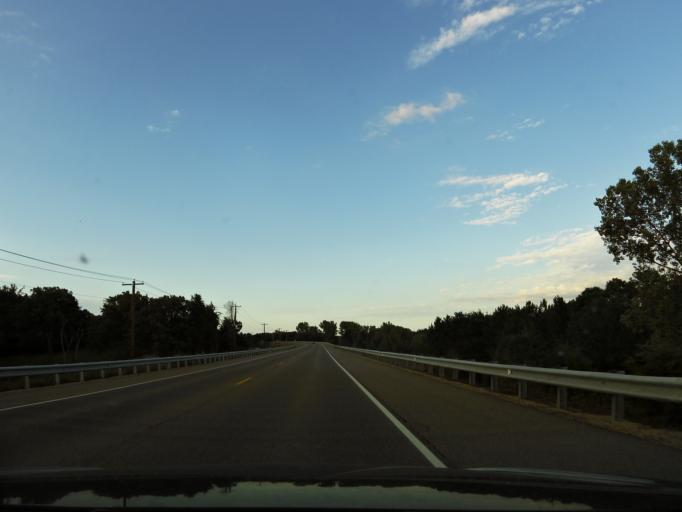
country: US
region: Minnesota
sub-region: Washington County
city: Cottage Grove
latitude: 44.8121
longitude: -92.9068
